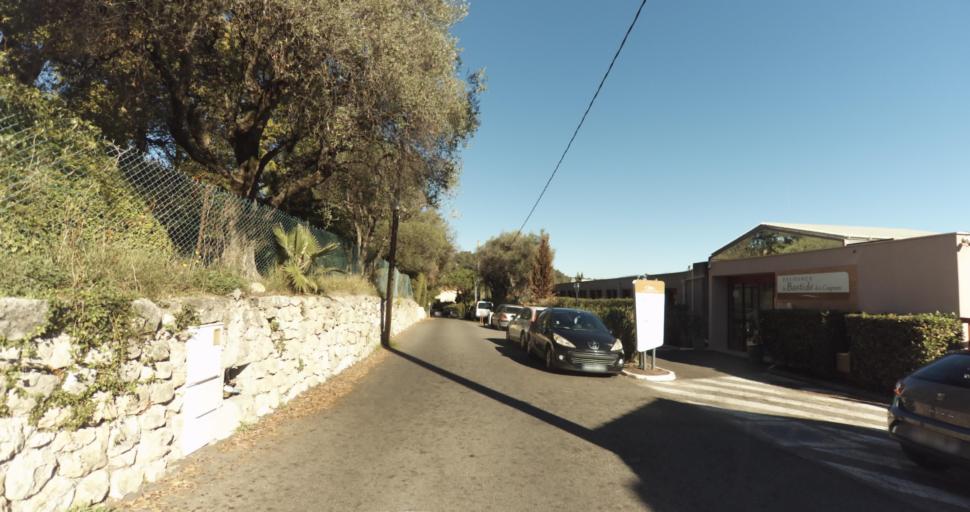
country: FR
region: Provence-Alpes-Cote d'Azur
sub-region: Departement des Alpes-Maritimes
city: Saint-Paul-de-Vence
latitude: 43.7037
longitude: 7.1316
